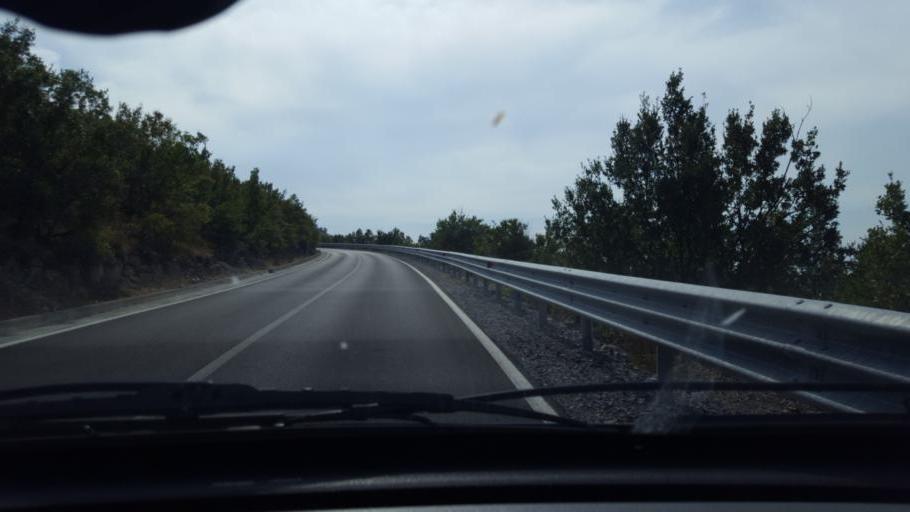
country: AL
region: Shkoder
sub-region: Rrethi i Malesia e Madhe
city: Hot
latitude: 42.3718
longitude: 19.4673
